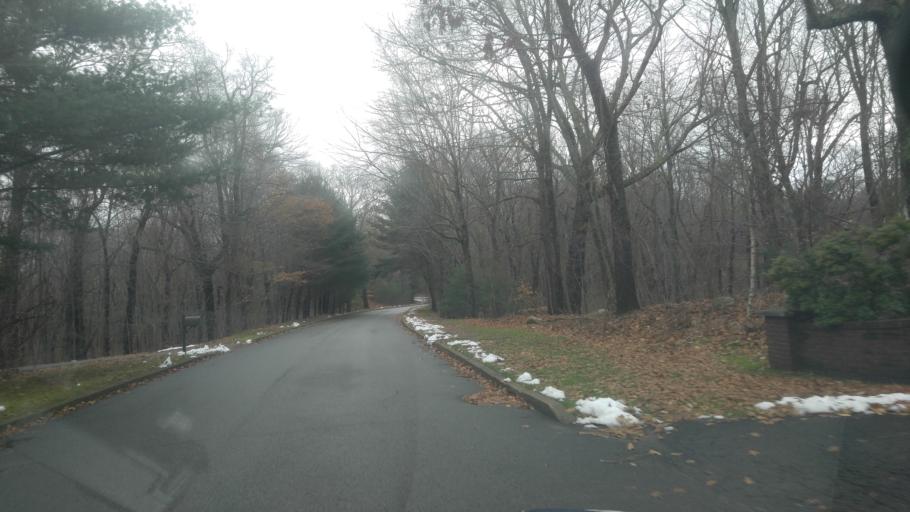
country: US
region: Rhode Island
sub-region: Kent County
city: West Warwick
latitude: 41.6533
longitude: -71.5376
